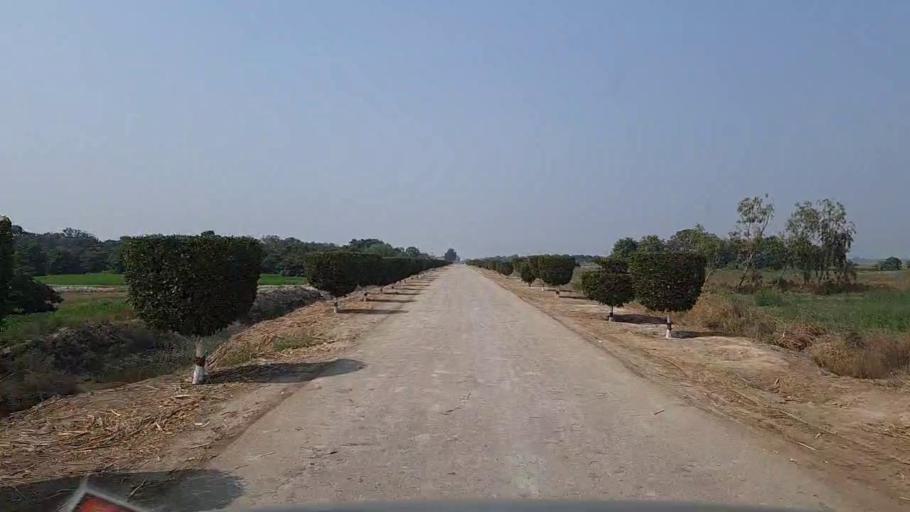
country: PK
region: Sindh
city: Mirwah Gorchani
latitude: 25.3358
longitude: 68.9982
